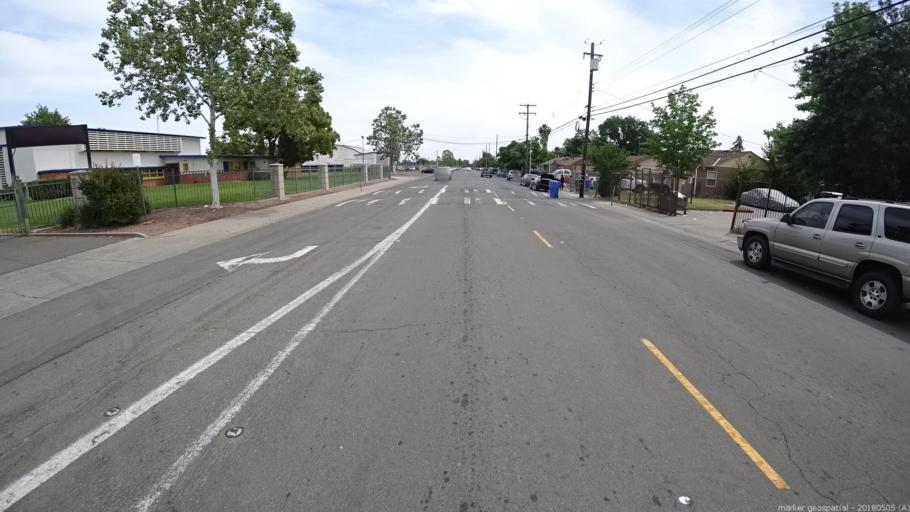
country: US
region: California
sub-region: Sacramento County
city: Rio Linda
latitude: 38.6330
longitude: -121.4382
